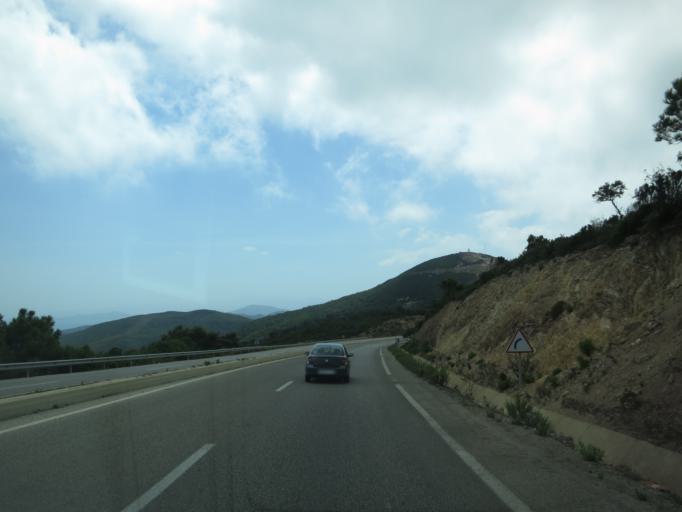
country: ES
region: Ceuta
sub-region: Ceuta
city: Ceuta
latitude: 35.8725
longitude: -5.4059
